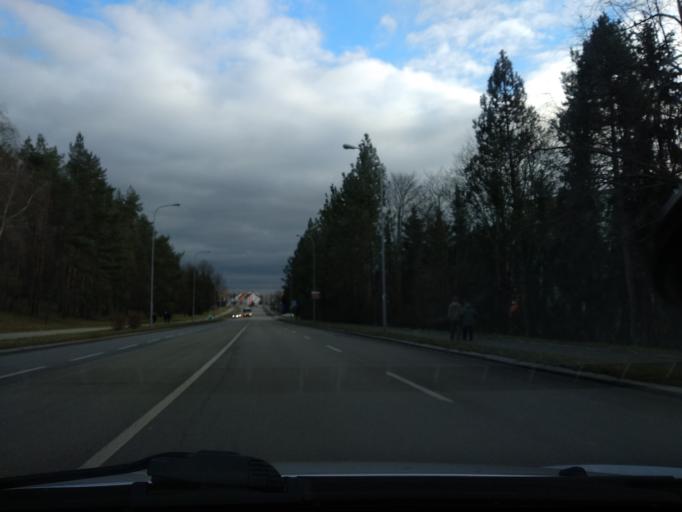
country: CZ
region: South Moravian
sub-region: Mesto Brno
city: Brno
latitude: 49.2256
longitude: 16.6184
